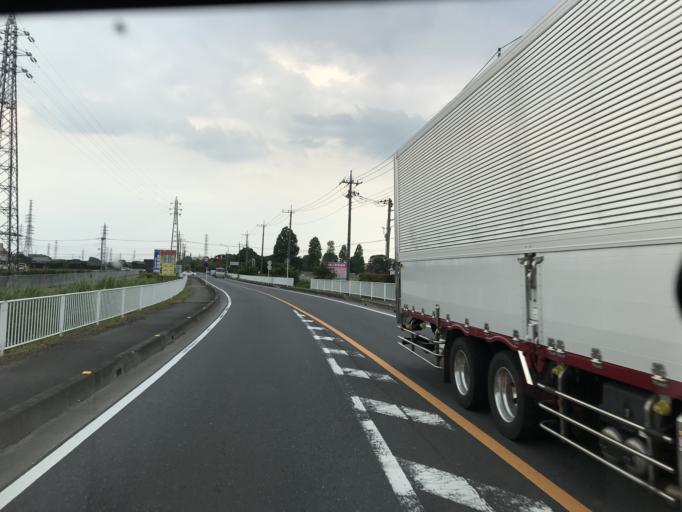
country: JP
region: Saitama
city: Shiraoka
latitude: 36.0183
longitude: 139.6788
